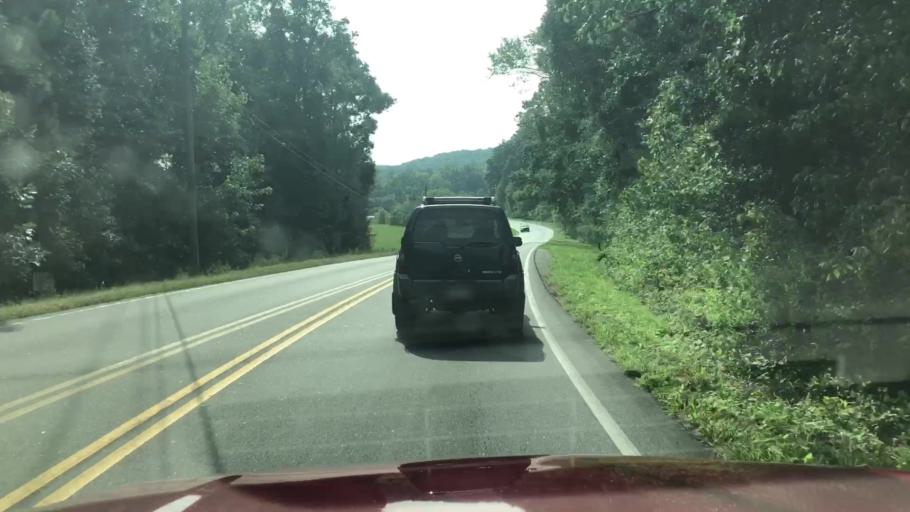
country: US
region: Georgia
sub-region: Bartow County
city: Cartersville
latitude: 34.1171
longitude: -84.8192
